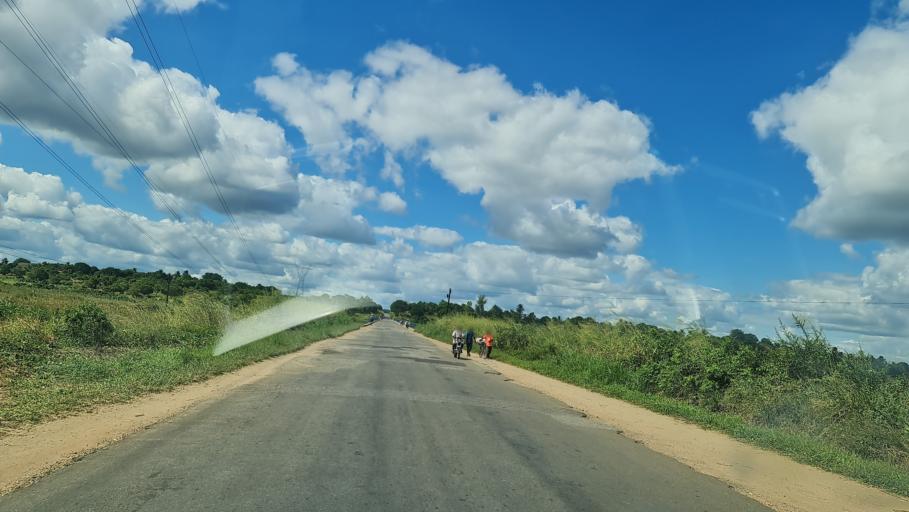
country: MZ
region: Zambezia
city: Quelimane
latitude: -17.5249
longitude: 36.2702
